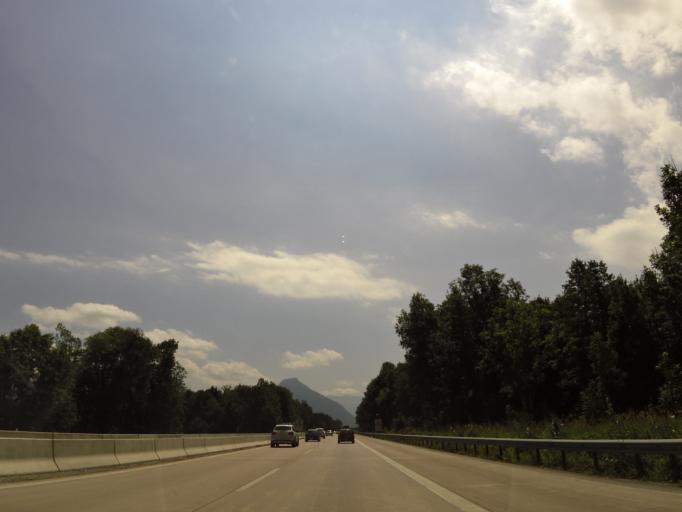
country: DE
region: Bavaria
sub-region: Upper Bavaria
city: Brannenburg
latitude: 47.7570
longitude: 12.1104
